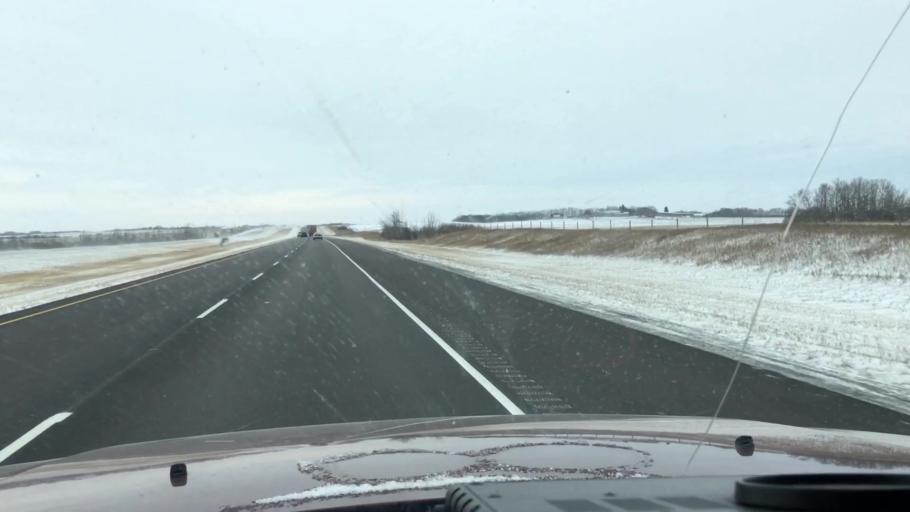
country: CA
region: Saskatchewan
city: Saskatoon
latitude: 51.6956
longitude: -106.4596
